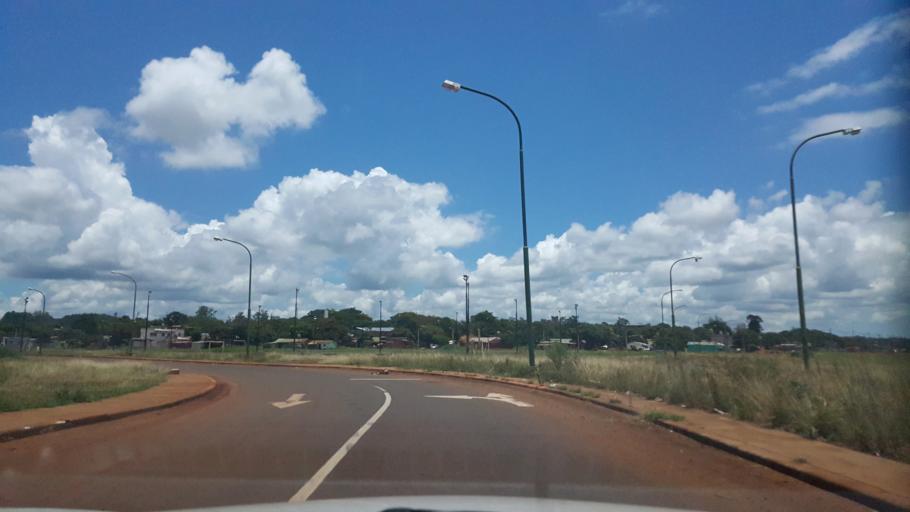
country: AR
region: Misiones
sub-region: Departamento de Capital
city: Posadas
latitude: -27.4210
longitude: -55.8900
